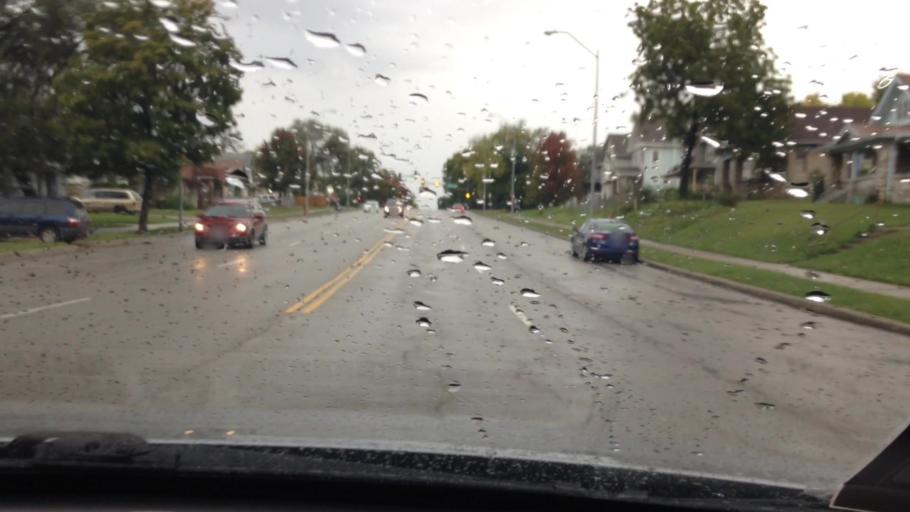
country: US
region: Missouri
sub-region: Jackson County
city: Kansas City
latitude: 39.0543
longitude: -94.5675
